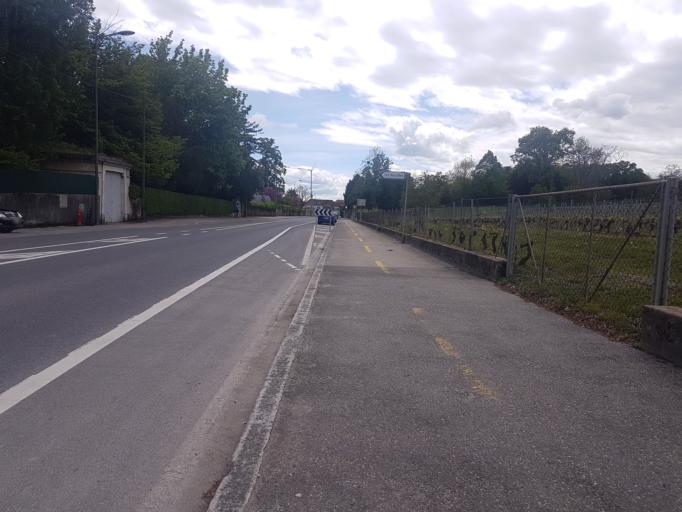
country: CH
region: Vaud
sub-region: Nyon District
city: Coppet
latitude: 46.3202
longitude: 6.1957
